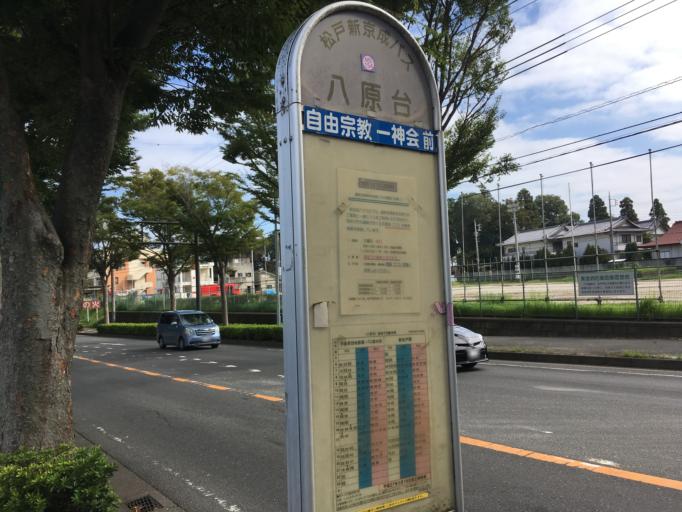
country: JP
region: Chiba
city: Matsudo
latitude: 35.8092
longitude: 139.9407
